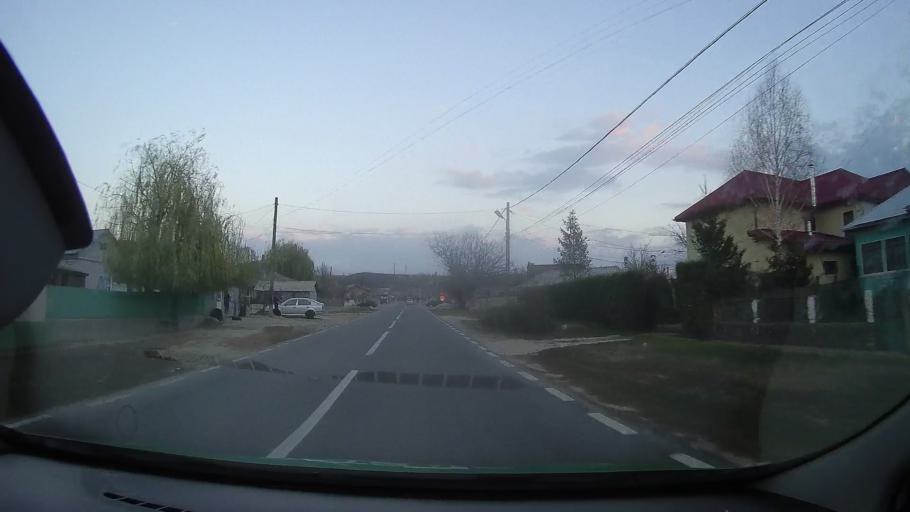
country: RO
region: Constanta
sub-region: Comuna Baneasa
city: Baneasa
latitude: 44.0749
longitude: 27.6870
